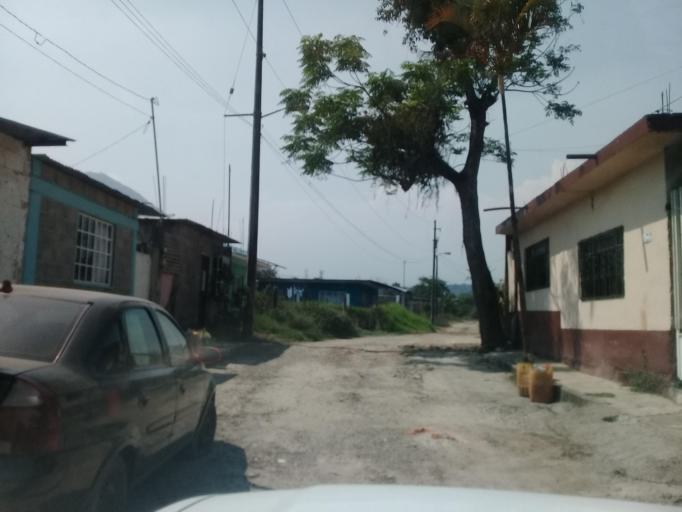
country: MX
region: Veracruz
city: Ixtac Zoquitlan
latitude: 18.8720
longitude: -97.0595
